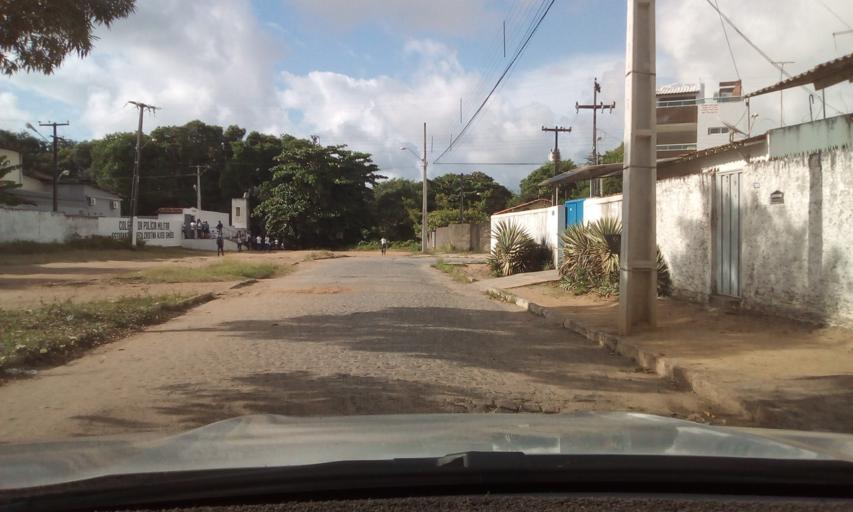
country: BR
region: Paraiba
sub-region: Joao Pessoa
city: Joao Pessoa
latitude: -7.1711
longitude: -34.8287
